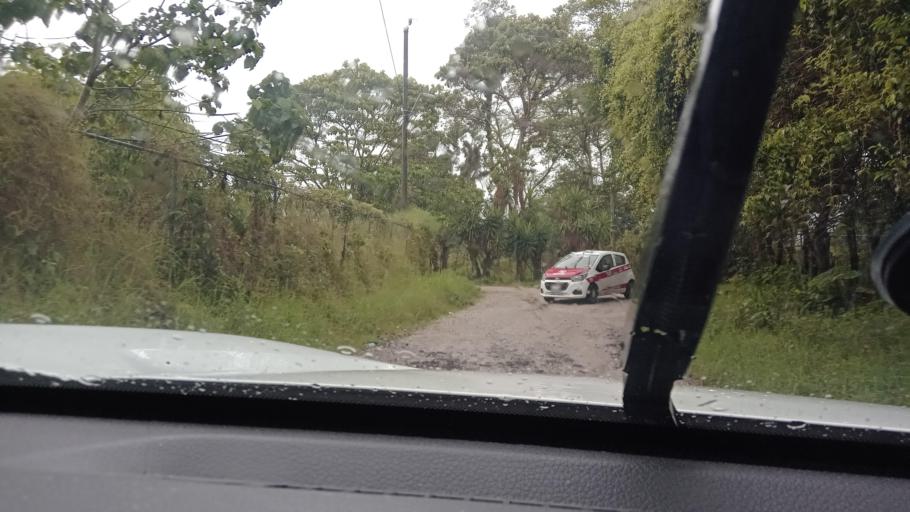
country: MX
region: Veracruz
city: Coatepec
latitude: 19.4566
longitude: -96.9778
